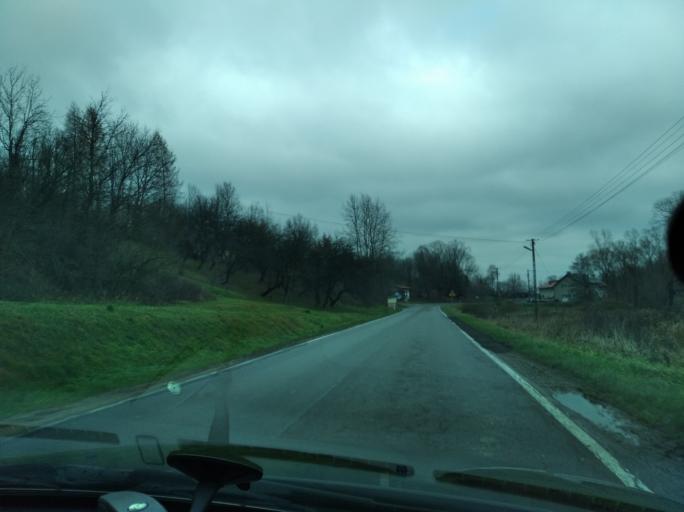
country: PL
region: Subcarpathian Voivodeship
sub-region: Powiat przeworski
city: Manasterz
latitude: 49.9267
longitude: 22.3357
